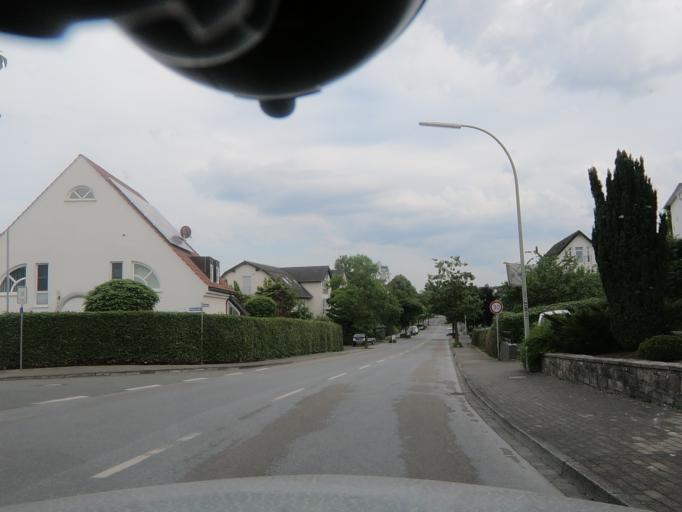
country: DE
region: North Rhine-Westphalia
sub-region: Regierungsbezirk Arnsberg
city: Ruthen
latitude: 51.4518
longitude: 8.4239
